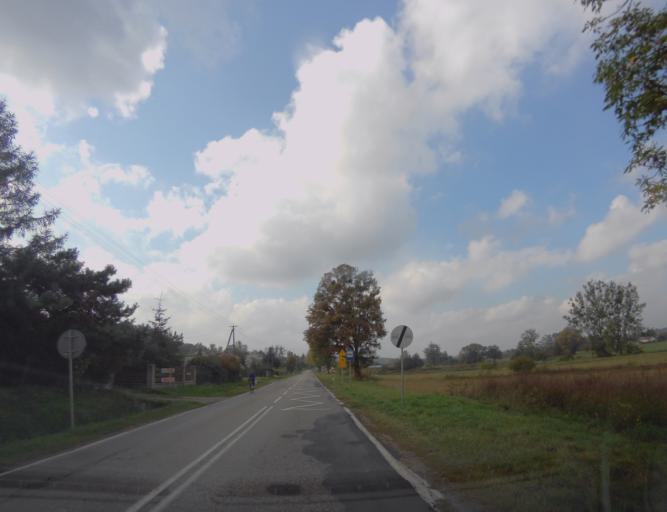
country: PL
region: Lublin Voivodeship
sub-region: Powiat krasnostawski
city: Krasnystaw
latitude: 50.9694
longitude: 23.1318
